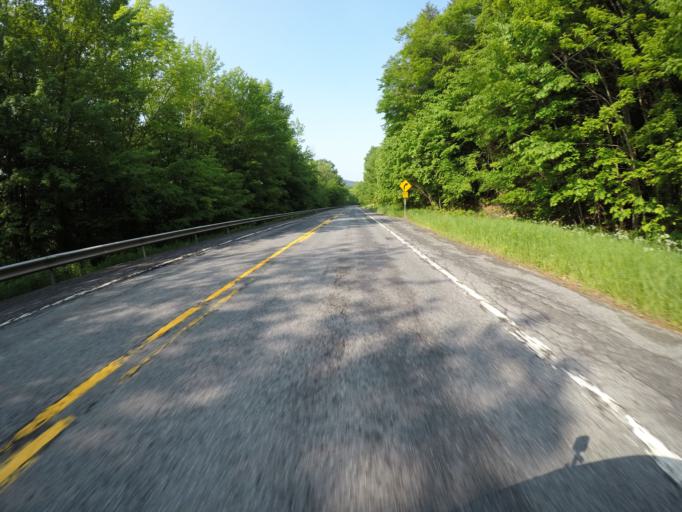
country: US
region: New York
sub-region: Sullivan County
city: Livingston Manor
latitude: 42.1230
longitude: -74.7246
